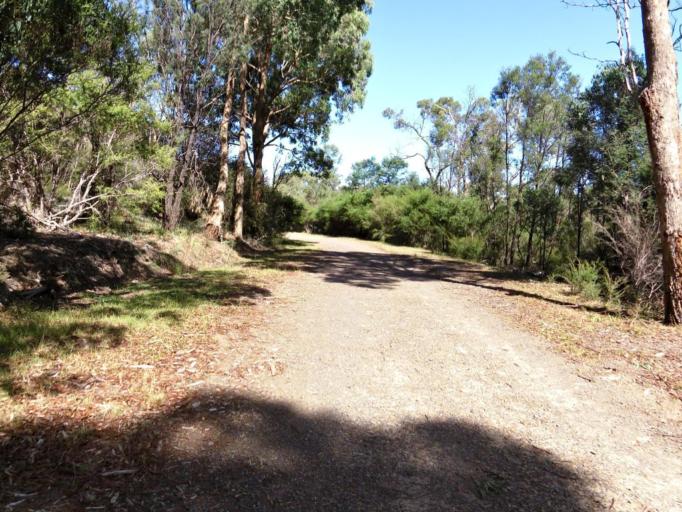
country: AU
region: Victoria
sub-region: Knox
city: Rowville
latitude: -37.9479
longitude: 145.2463
